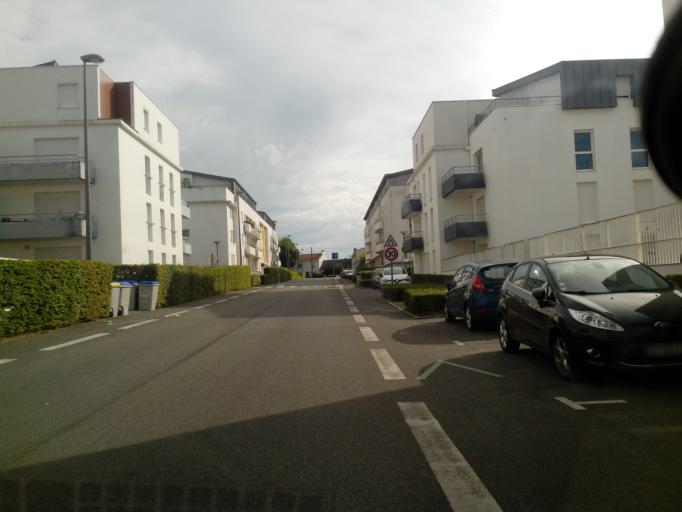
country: FR
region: Pays de la Loire
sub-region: Departement de la Loire-Atlantique
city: Nantes
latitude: 47.2540
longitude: -1.5792
